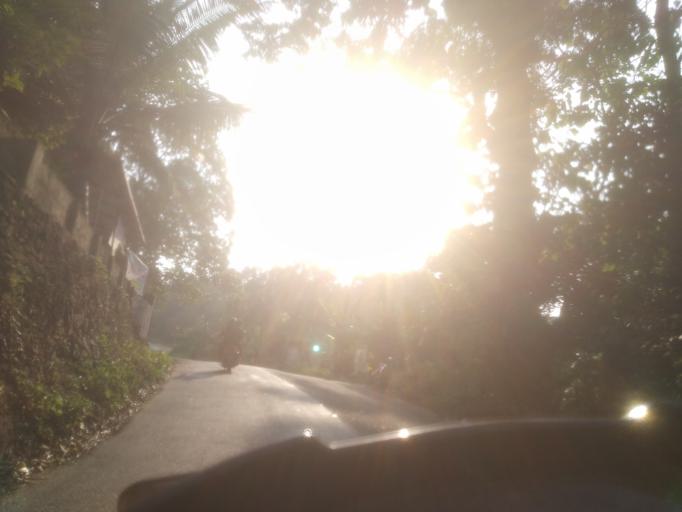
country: IN
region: Kerala
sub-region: Ernakulam
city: Piravam
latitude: 9.8119
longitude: 76.4979
